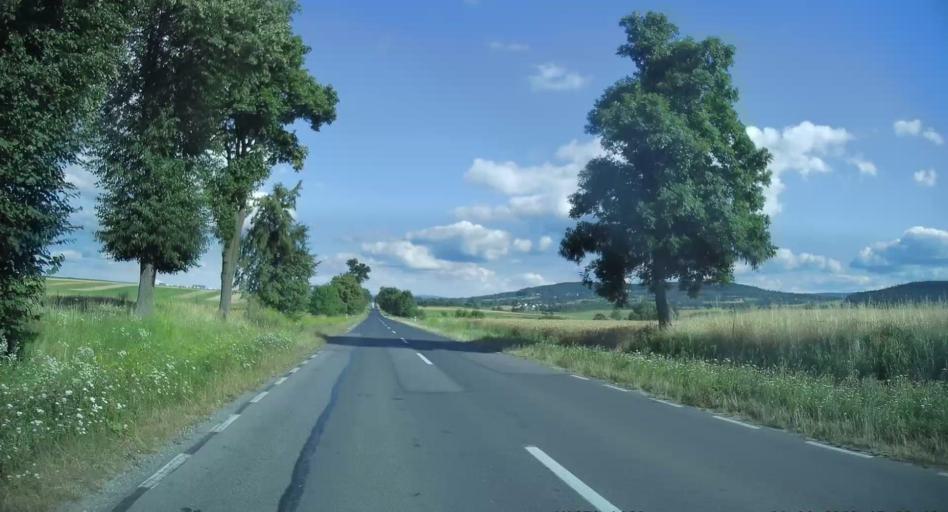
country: PL
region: Swietokrzyskie
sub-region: Powiat kielecki
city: Bodzentyn
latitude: 50.9555
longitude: 20.9162
